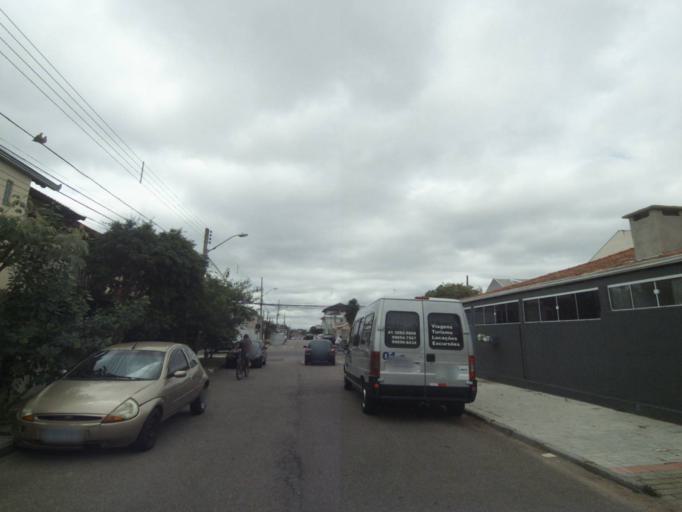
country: BR
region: Parana
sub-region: Sao Jose Dos Pinhais
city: Sao Jose dos Pinhais
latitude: -25.5443
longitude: -49.2589
